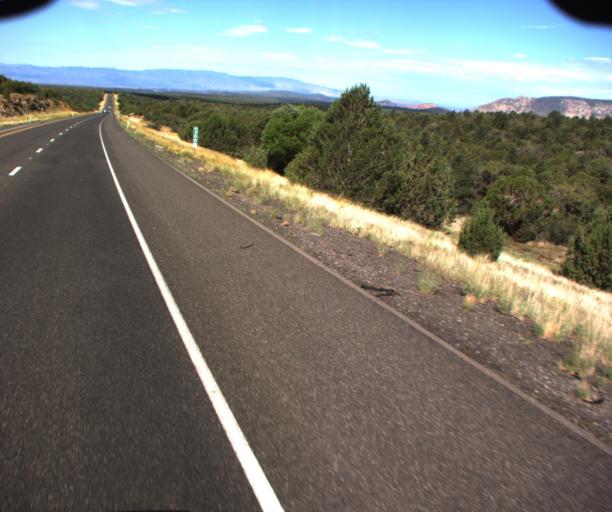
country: US
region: Arizona
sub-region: Yavapai County
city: Village of Oak Creek (Big Park)
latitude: 34.7822
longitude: -111.6151
